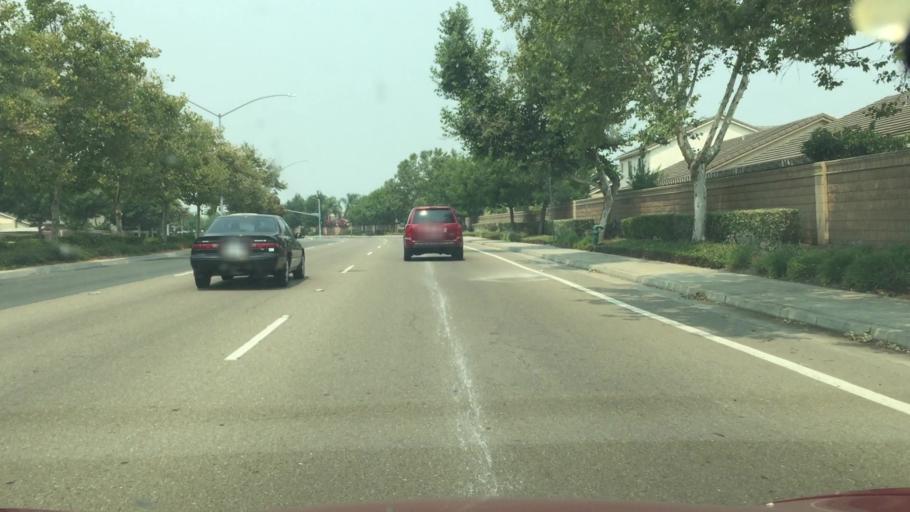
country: US
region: California
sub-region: San Joaquin County
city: Morada
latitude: 38.0254
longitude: -121.2703
